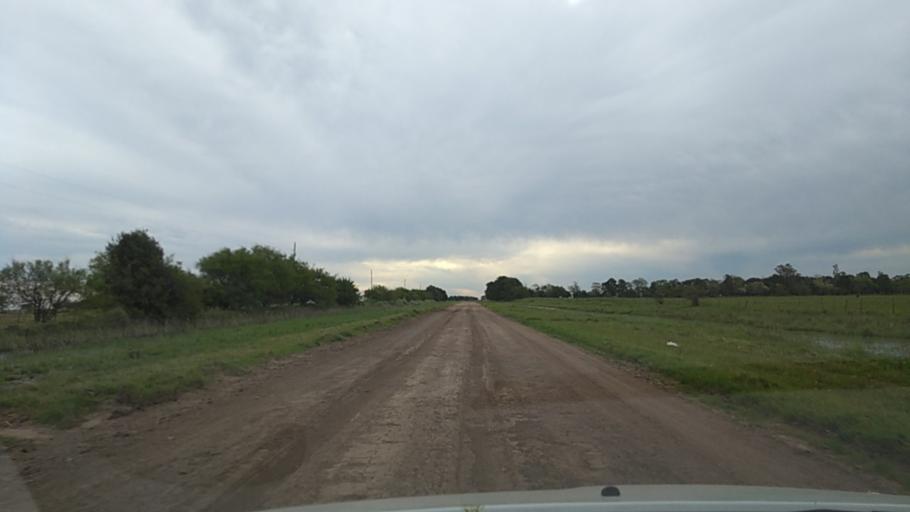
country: AR
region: Buenos Aires
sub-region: Partido de General Madariaga
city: General Juan Madariaga
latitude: -36.9663
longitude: -57.1822
